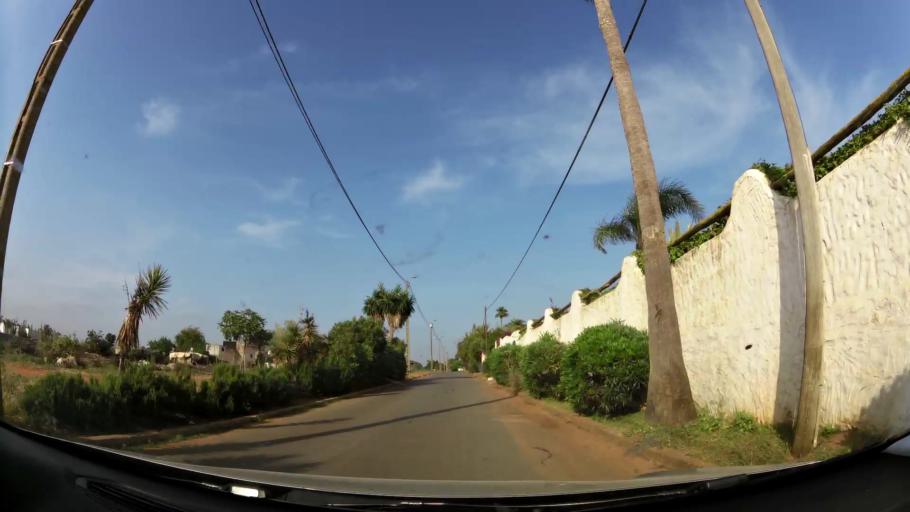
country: MA
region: Rabat-Sale-Zemmour-Zaer
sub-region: Rabat
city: Rabat
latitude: 33.9399
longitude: -6.8119
